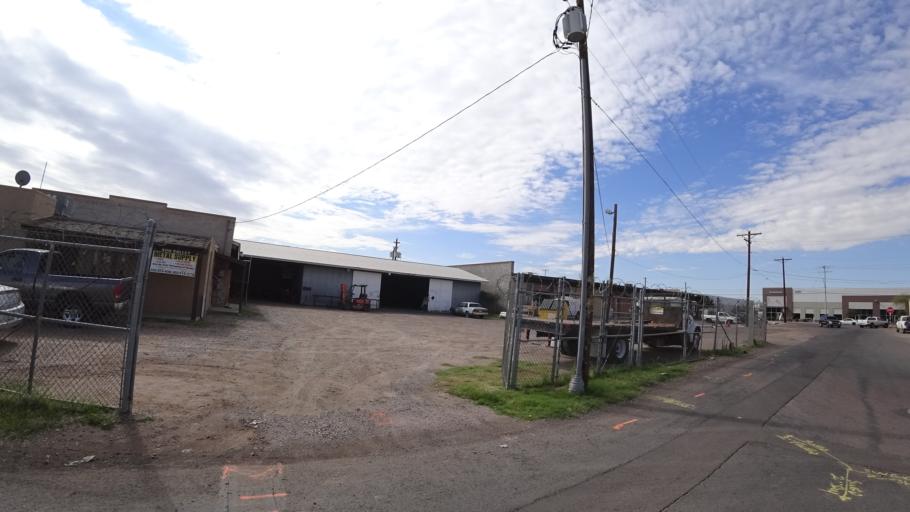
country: US
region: Arizona
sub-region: Maricopa County
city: Phoenix
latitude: 33.4272
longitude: -112.0815
